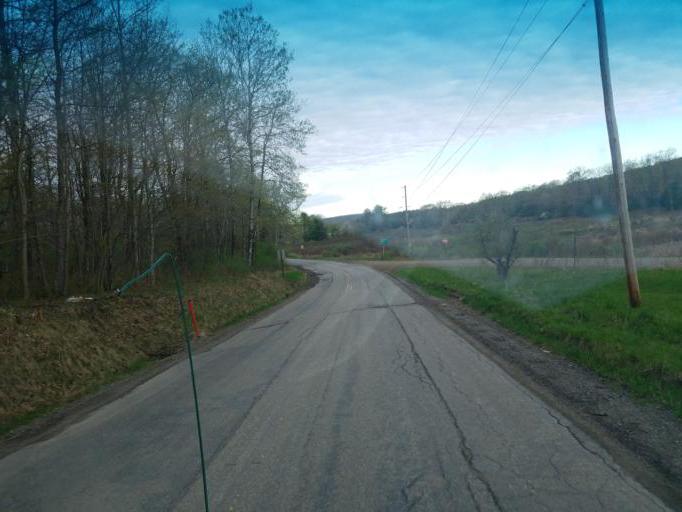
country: US
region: New York
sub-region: Allegany County
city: Andover
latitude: 41.9859
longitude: -77.7471
